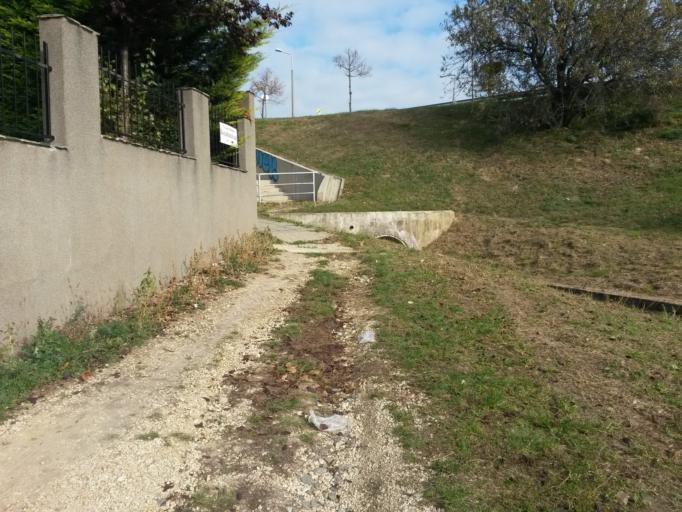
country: HU
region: Budapest
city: Budapest XII. keruelet
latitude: 47.4732
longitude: 18.9914
